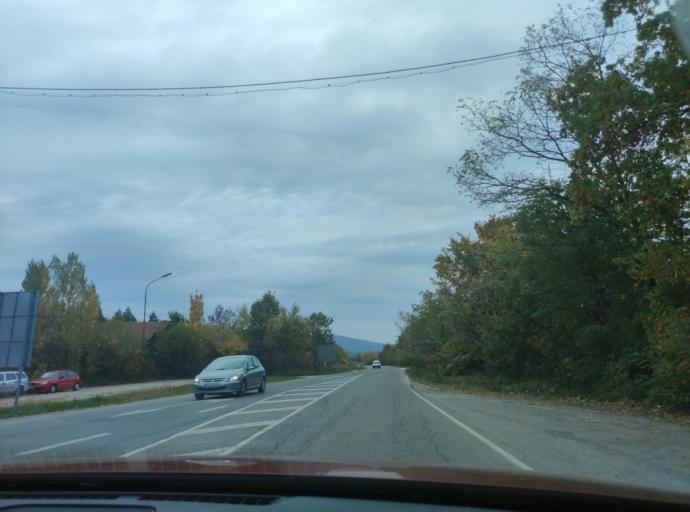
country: BG
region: Montana
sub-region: Obshtina Berkovitsa
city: Berkovitsa
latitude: 43.2196
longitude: 23.1595
